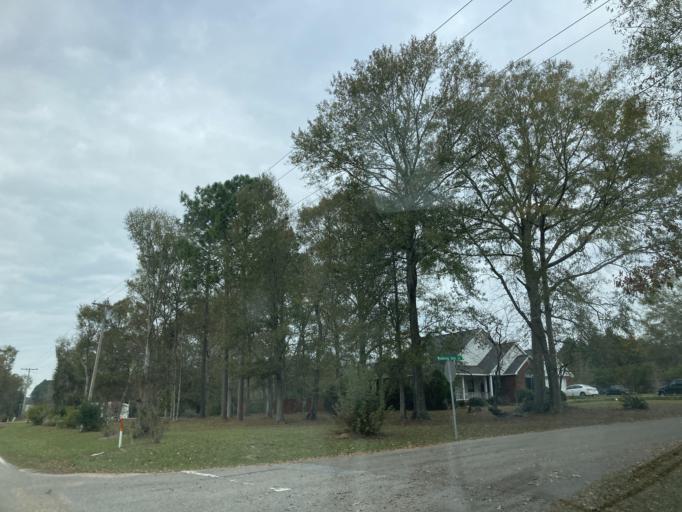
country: US
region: Mississippi
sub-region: Lamar County
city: Purvis
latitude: 31.1443
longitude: -89.2635
